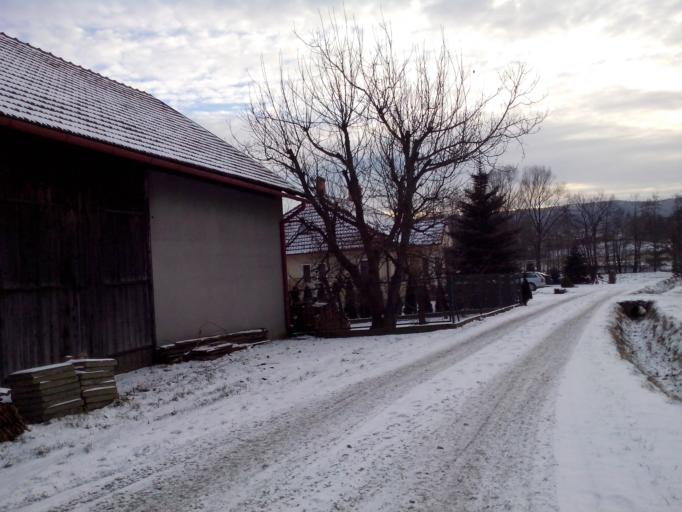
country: PL
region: Subcarpathian Voivodeship
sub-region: Powiat strzyzowski
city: Strzyzow
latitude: 49.8497
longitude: 21.8126
